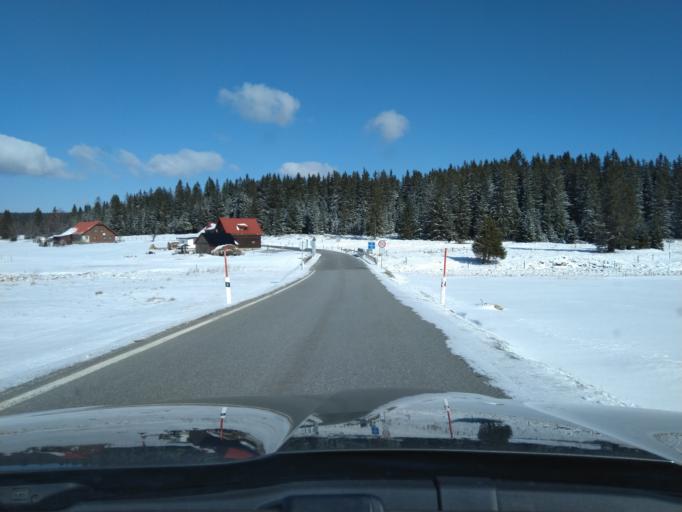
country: CZ
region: Plzensky
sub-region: Okres Klatovy
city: Kasperske Hory
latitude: 49.0476
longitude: 13.5775
